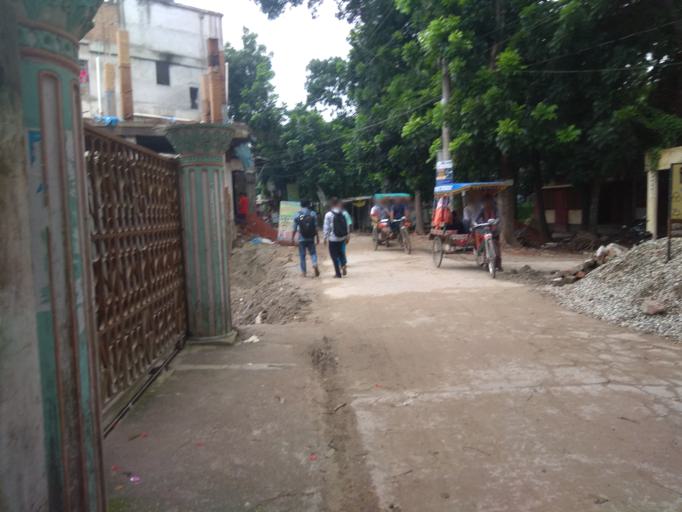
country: BD
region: Dhaka
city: Dohar
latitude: 23.4730
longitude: 90.0263
